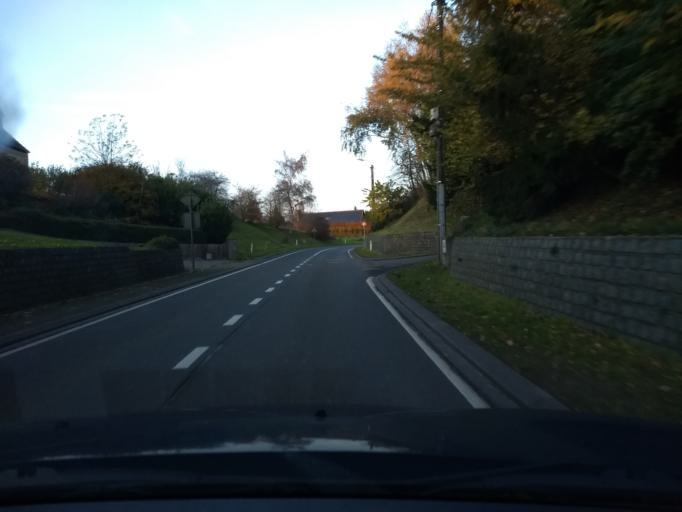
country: BE
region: Wallonia
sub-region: Province du Brabant Wallon
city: Ittre
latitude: 50.6538
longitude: 4.2984
